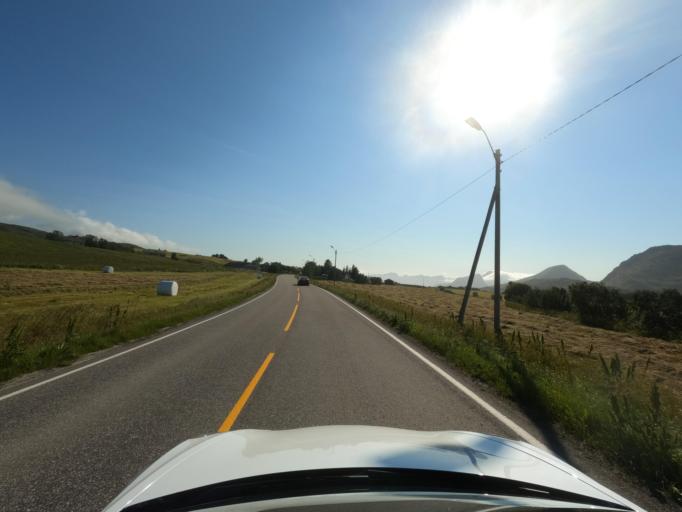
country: NO
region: Nordland
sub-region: Vestvagoy
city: Evjen
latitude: 68.2056
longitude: 13.6853
